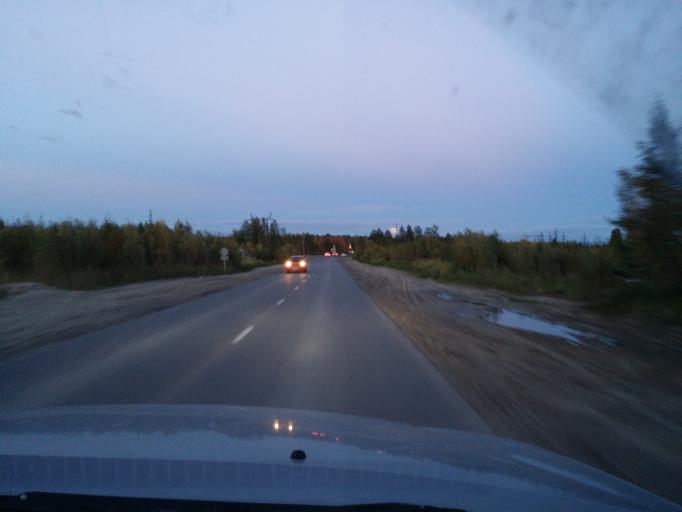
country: RU
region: Khanty-Mansiyskiy Avtonomnyy Okrug
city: Nizhnevartovsk
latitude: 60.9919
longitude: 76.4299
